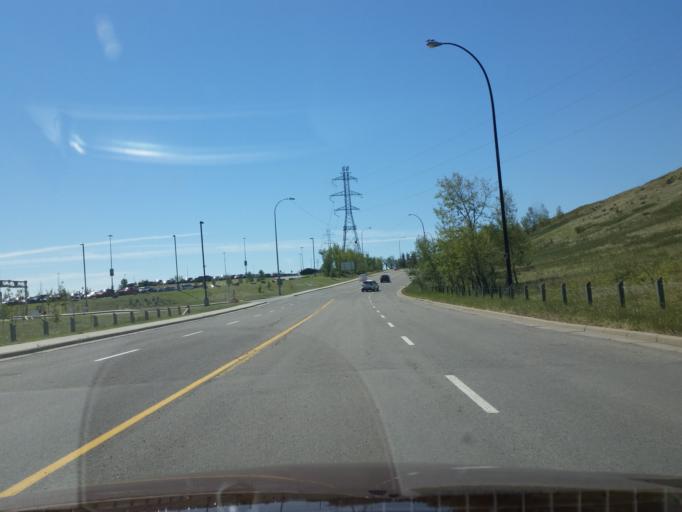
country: CA
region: Alberta
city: Calgary
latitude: 51.0520
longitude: -114.0256
